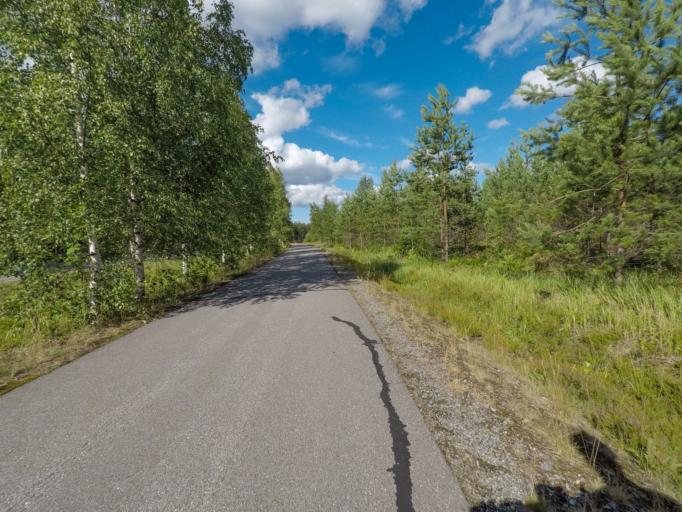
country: FI
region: South Karelia
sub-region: Lappeenranta
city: Joutseno
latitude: 61.1470
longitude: 28.5498
